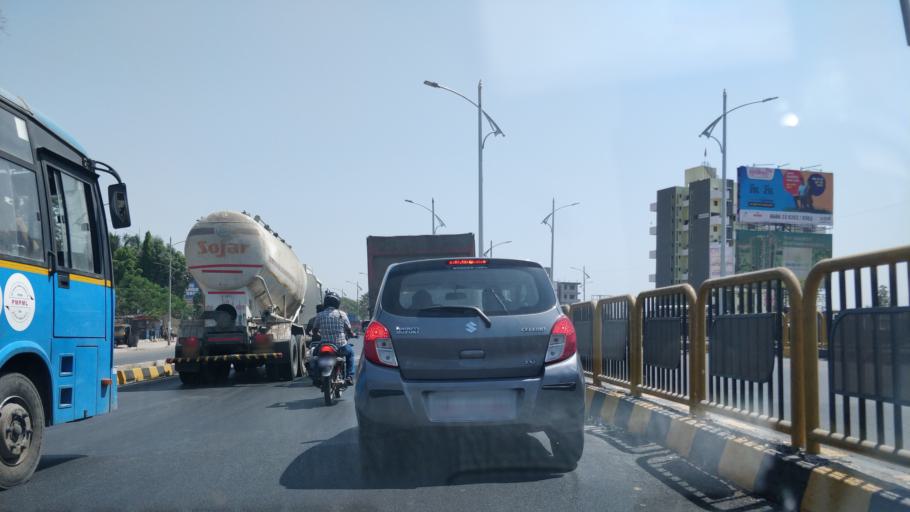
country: IN
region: Maharashtra
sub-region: Pune Division
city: Alandi
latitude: 18.6653
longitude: 73.8881
